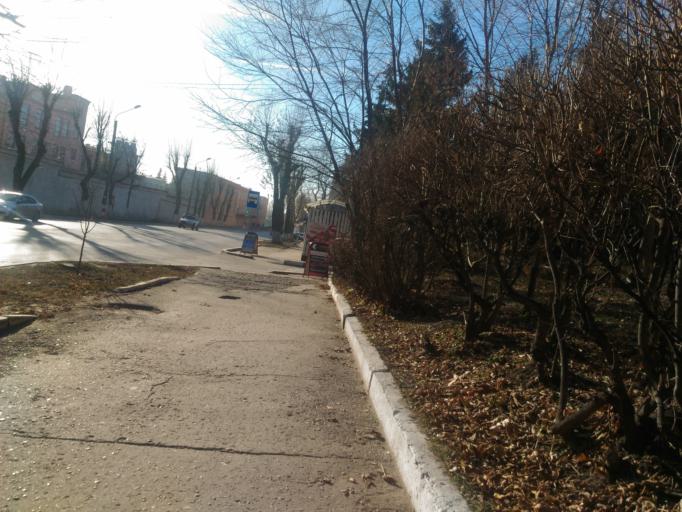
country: RU
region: Ulyanovsk
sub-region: Ulyanovskiy Rayon
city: Ulyanovsk
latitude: 54.3207
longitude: 48.3863
